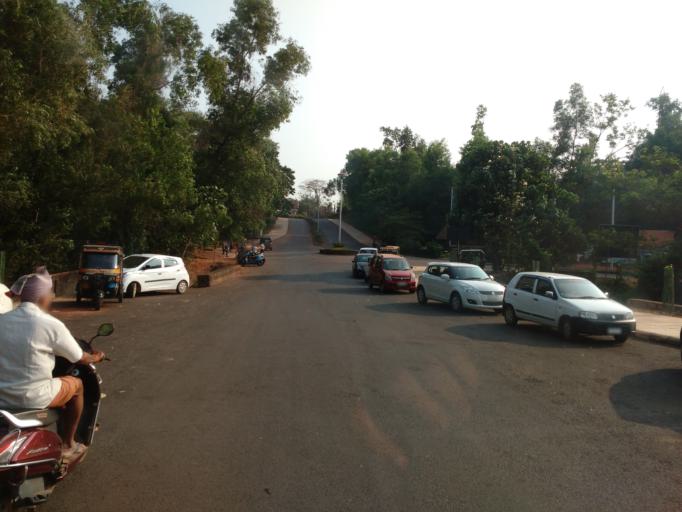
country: IN
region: Karnataka
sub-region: Dakshina Kannada
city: Mangalore
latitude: 12.9278
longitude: 74.8993
